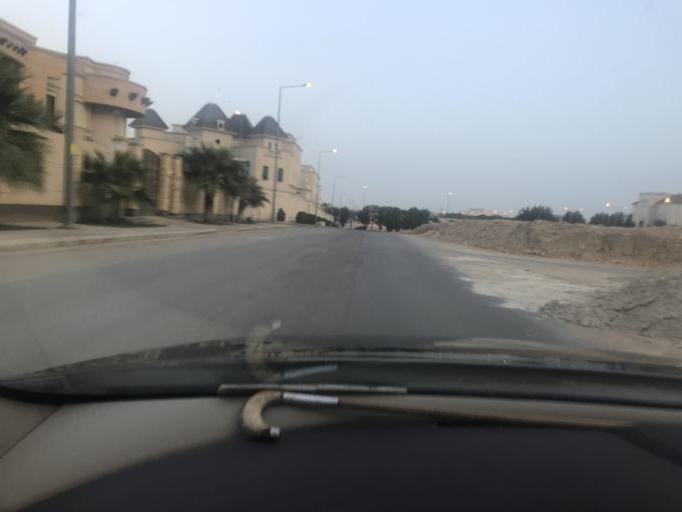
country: SA
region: Ar Riyad
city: Riyadh
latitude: 24.7268
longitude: 46.7491
